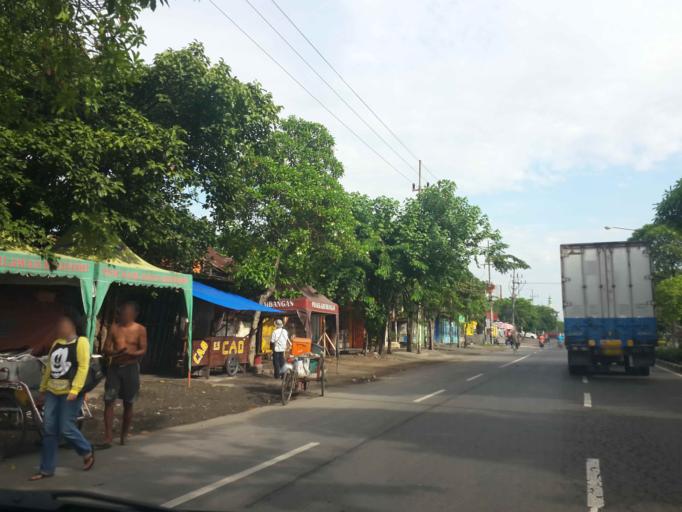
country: ID
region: East Java
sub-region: Kota Surabaya
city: Surabaya
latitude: -7.2436
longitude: 112.7208
